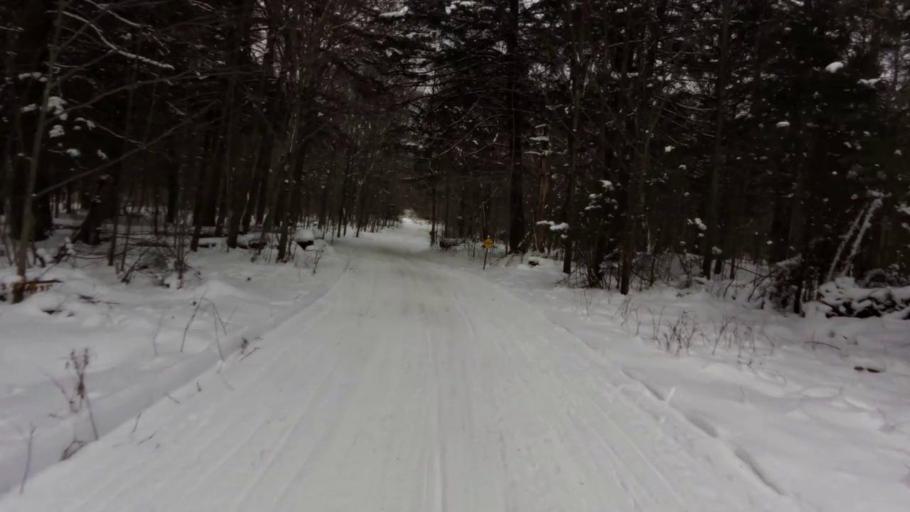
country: US
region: Pennsylvania
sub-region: McKean County
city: Bradford
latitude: 42.0197
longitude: -78.7224
